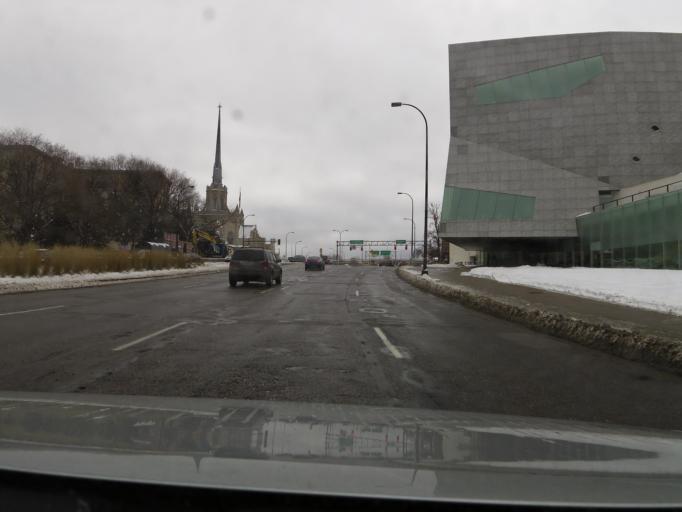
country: US
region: Minnesota
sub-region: Hennepin County
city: Minneapolis
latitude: 44.9685
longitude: -93.2881
